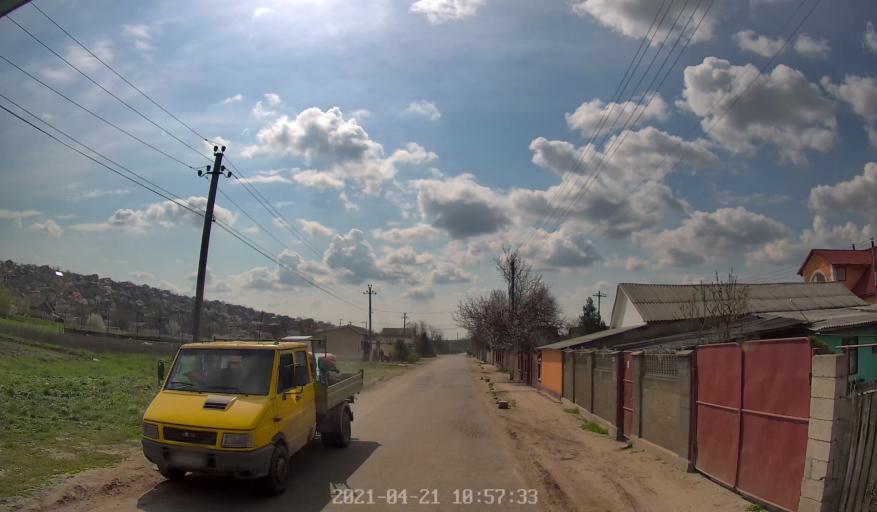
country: MD
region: Chisinau
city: Singera
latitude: 46.9592
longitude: 28.9395
